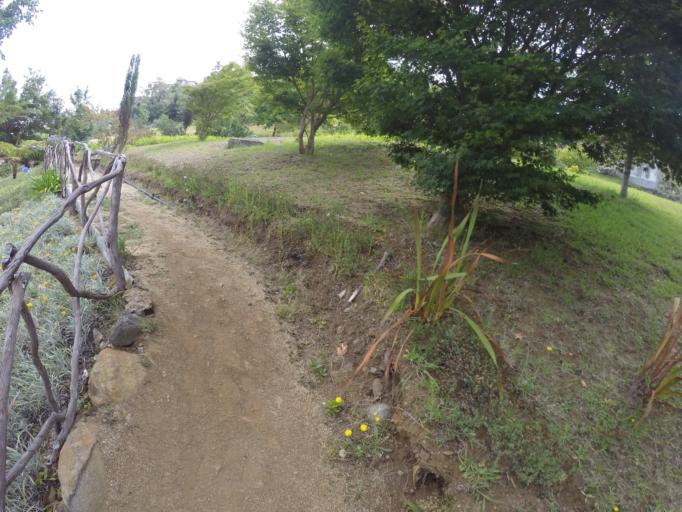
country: PT
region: Madeira
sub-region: Santana
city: Santana
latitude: 32.8027
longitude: -16.8845
